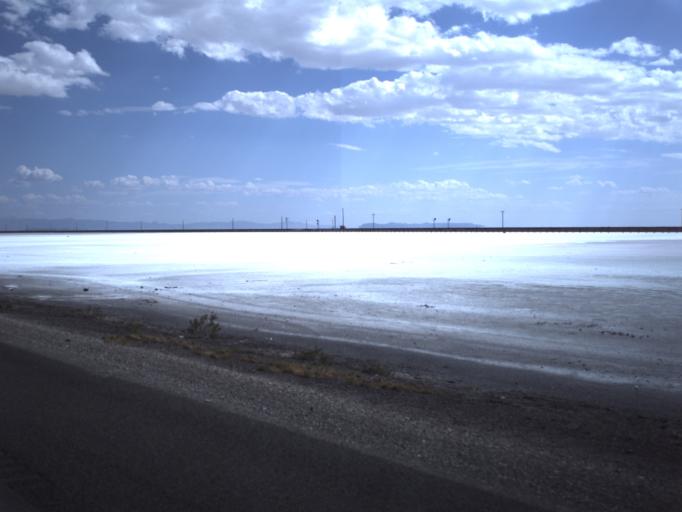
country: US
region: Utah
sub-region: Tooele County
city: Wendover
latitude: 40.7346
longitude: -113.6663
